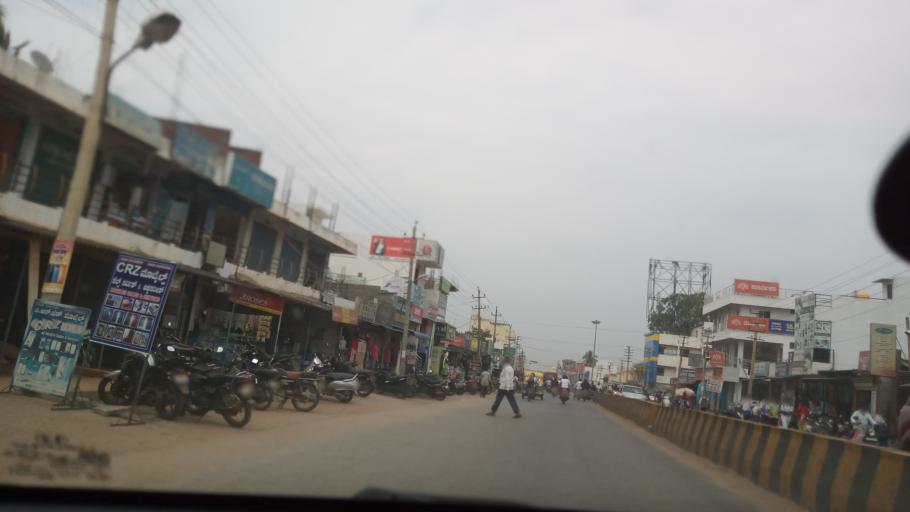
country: IN
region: Karnataka
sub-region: Chamrajnagar
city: Chamrajnagar
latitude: 11.9249
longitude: 76.9400
